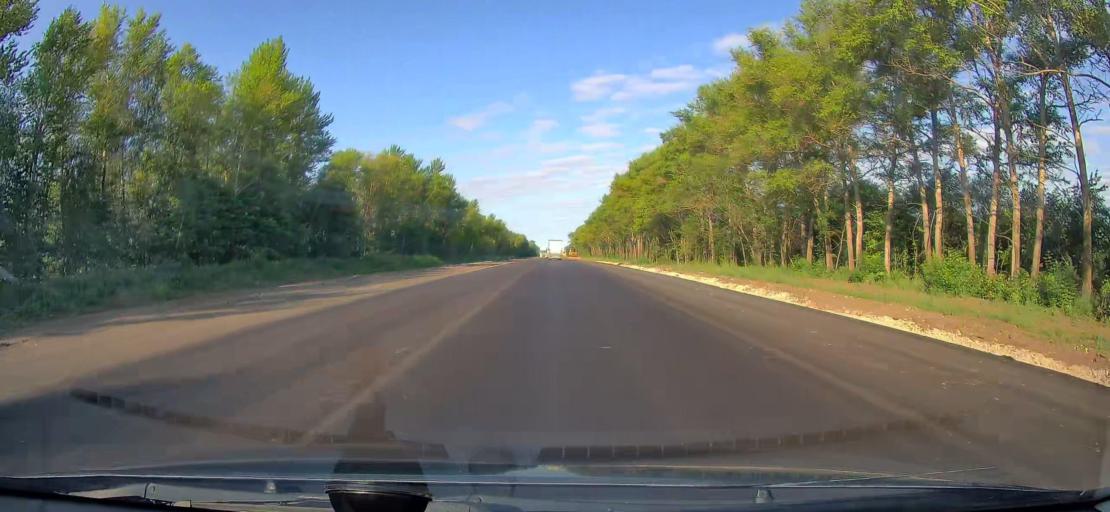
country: RU
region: Tula
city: Bol'shoye Skuratovo
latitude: 53.4387
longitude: 36.8201
